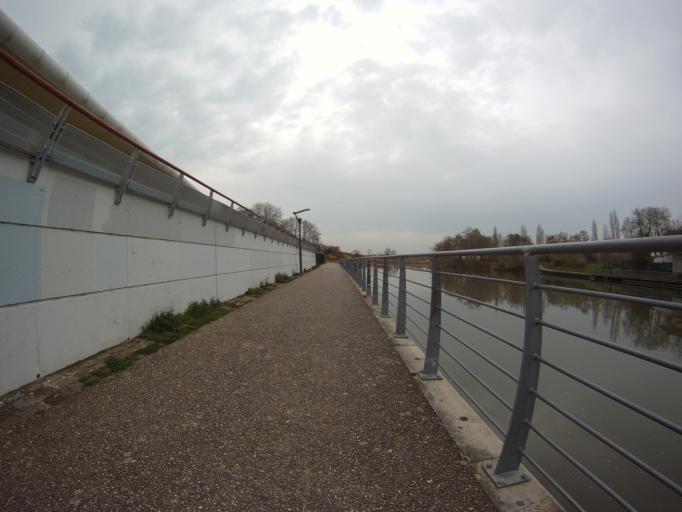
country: FR
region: Lorraine
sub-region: Departement de Meurthe-et-Moselle
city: Saint-Max
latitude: 48.6973
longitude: 6.2051
